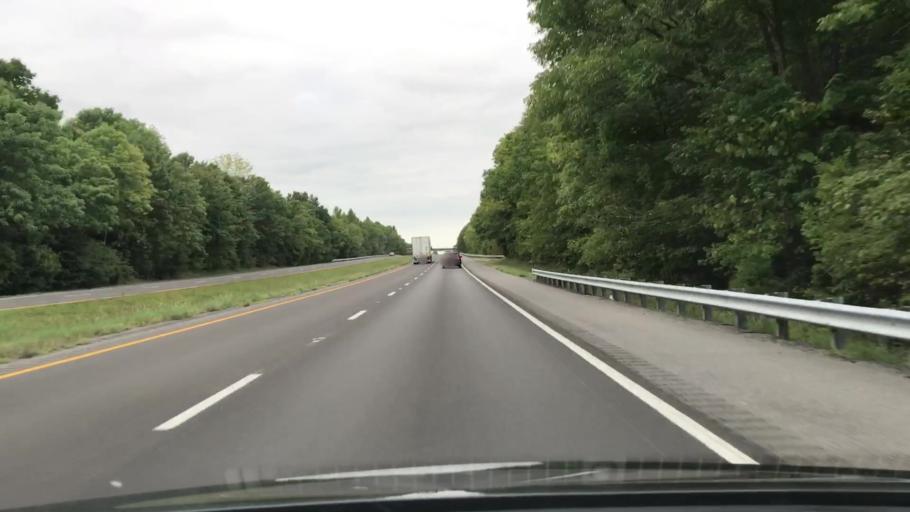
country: US
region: Kentucky
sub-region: Fulton County
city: Fulton
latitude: 36.6119
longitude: -88.7885
